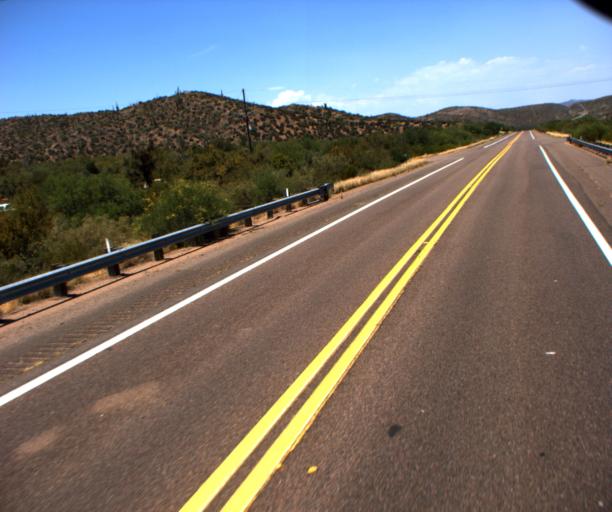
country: US
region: Arizona
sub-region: Gila County
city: Tonto Basin
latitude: 33.9636
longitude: -111.3250
